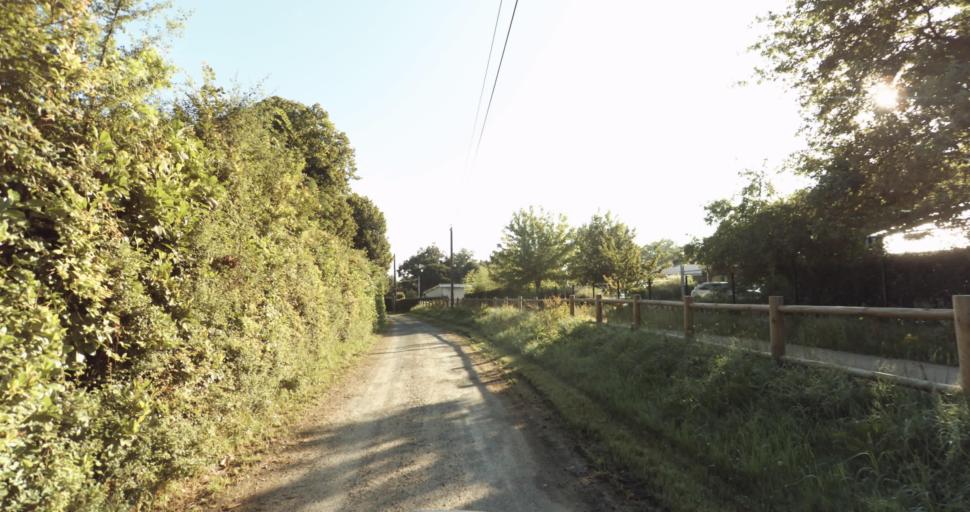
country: FR
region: Aquitaine
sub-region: Departement de la Gironde
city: Bazas
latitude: 44.4267
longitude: -0.2225
